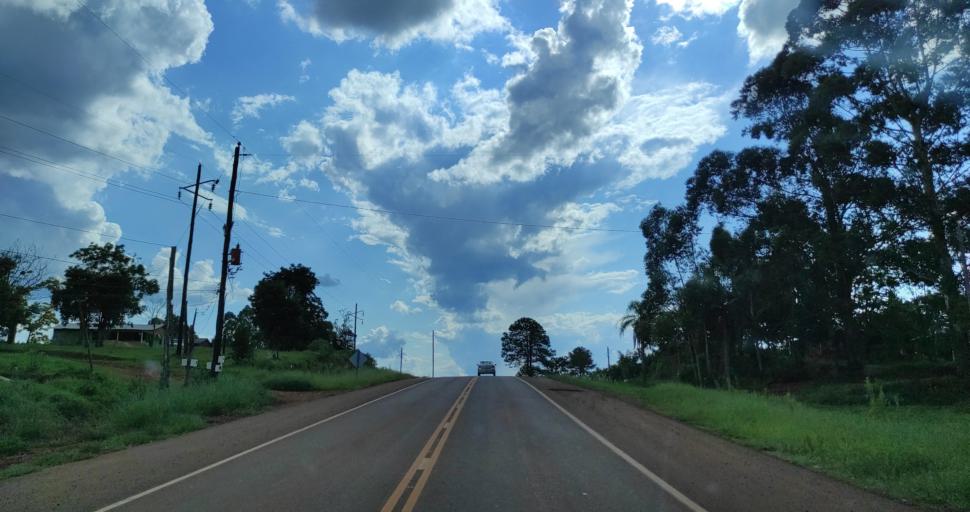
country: AR
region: Misiones
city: Bernardo de Irigoyen
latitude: -26.2932
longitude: -53.7711
